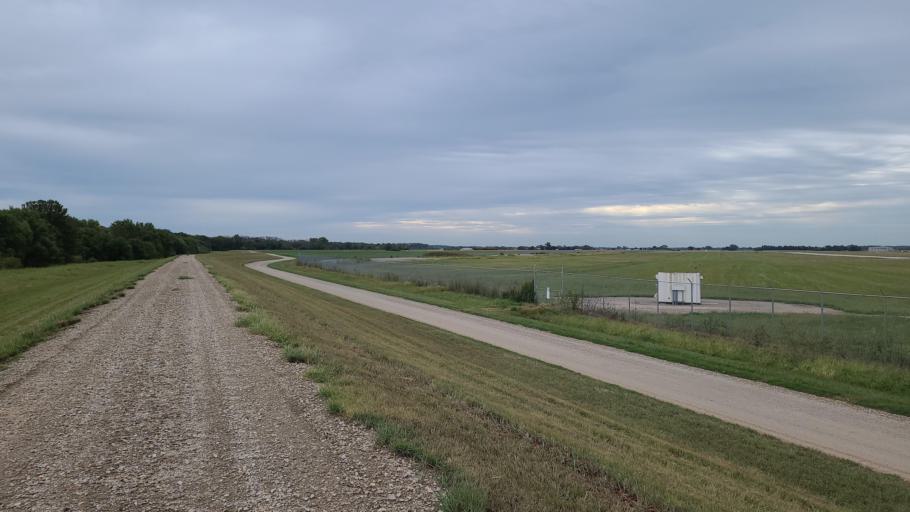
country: US
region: Kansas
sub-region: Douglas County
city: Lawrence
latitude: 39.0222
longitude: -95.2212
